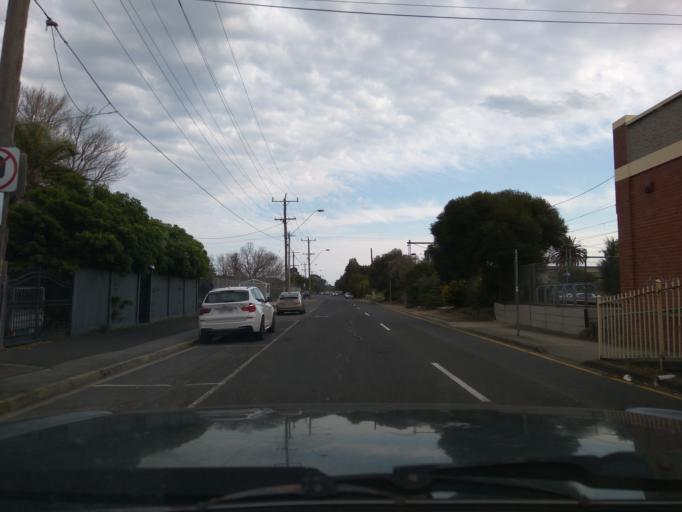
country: AU
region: Victoria
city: Spotswood
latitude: -37.8306
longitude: 144.8862
